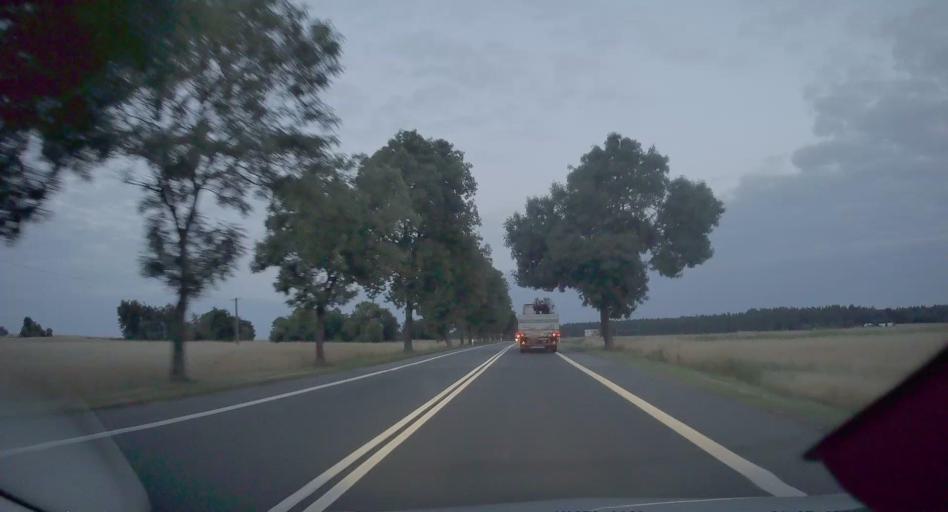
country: PL
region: Silesian Voivodeship
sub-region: Powiat klobucki
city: Opatow
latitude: 50.9491
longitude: 18.8267
